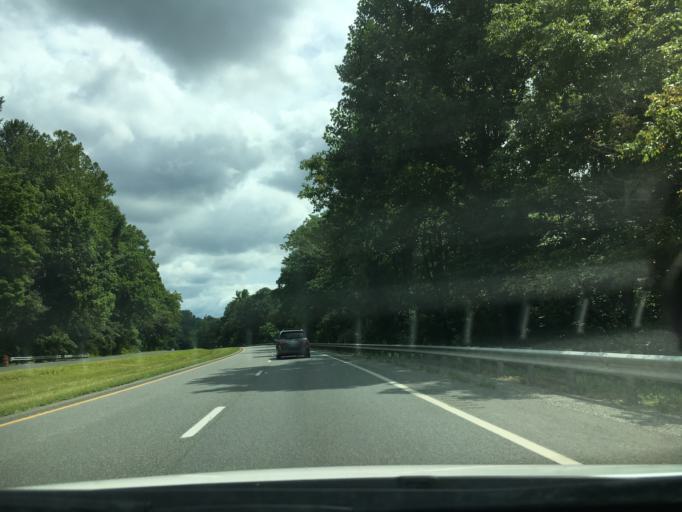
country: US
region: Virginia
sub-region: City of Charlottesville
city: Charlottesville
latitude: 38.0075
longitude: -78.5693
